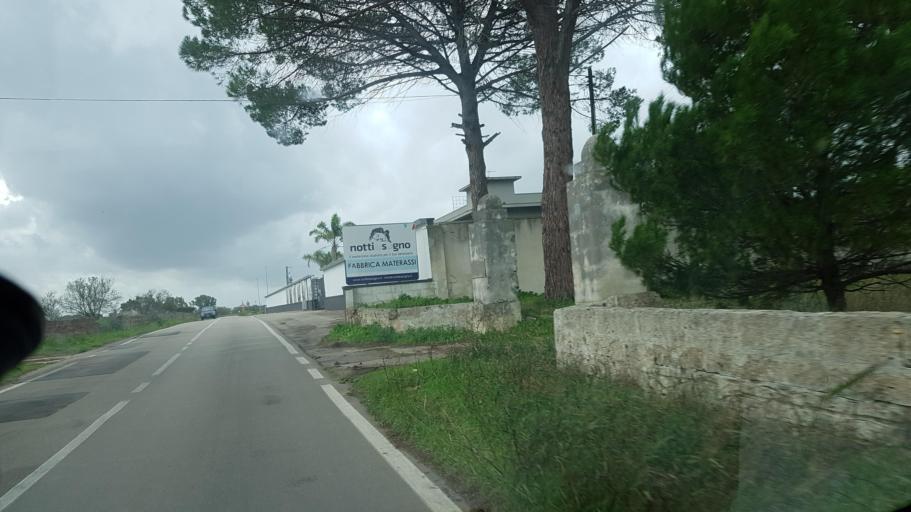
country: IT
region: Apulia
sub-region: Provincia di Lecce
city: Novoli
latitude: 40.3680
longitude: 18.0447
